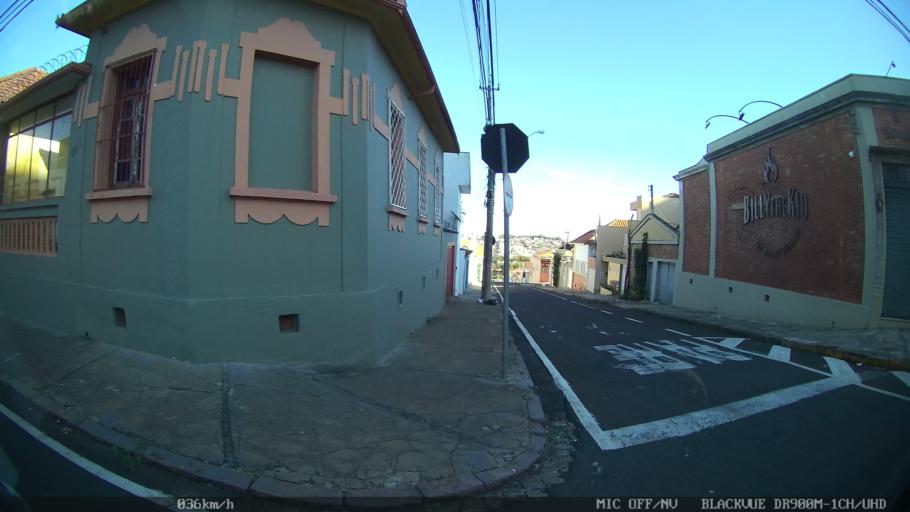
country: BR
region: Sao Paulo
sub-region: Franca
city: Franca
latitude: -20.5334
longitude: -47.4020
